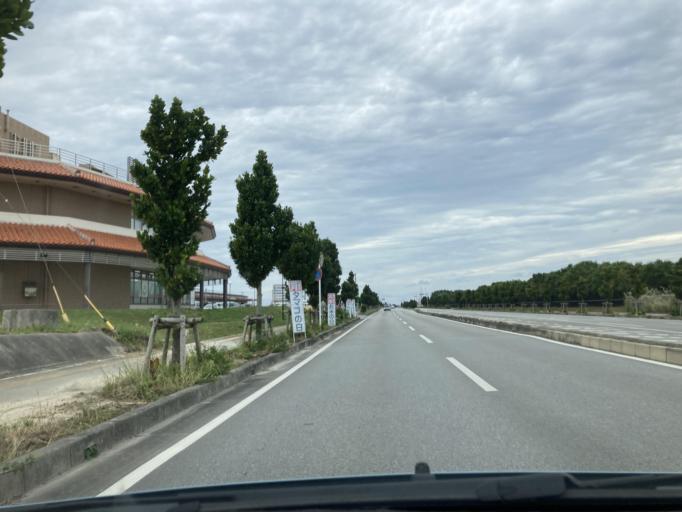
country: JP
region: Okinawa
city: Okinawa
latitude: 26.3934
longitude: 127.7466
